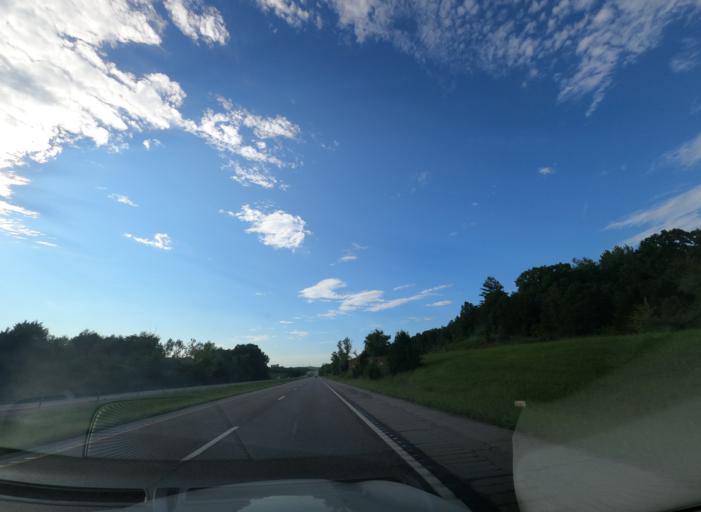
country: US
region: Missouri
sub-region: Jefferson County
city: Crystal City
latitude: 38.1765
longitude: -90.3787
